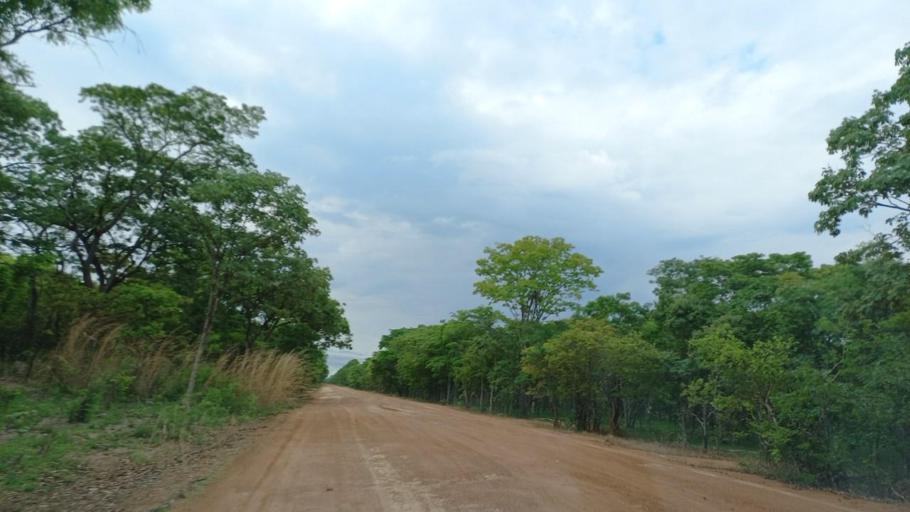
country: ZM
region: North-Western
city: Kalengwa
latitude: -13.3711
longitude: 25.0740
